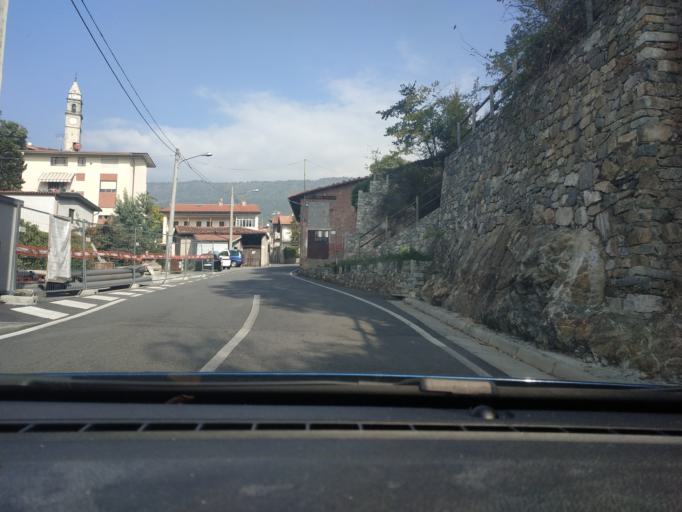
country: IT
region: Piedmont
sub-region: Provincia di Torino
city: Chiaverano
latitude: 45.4951
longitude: 7.9041
